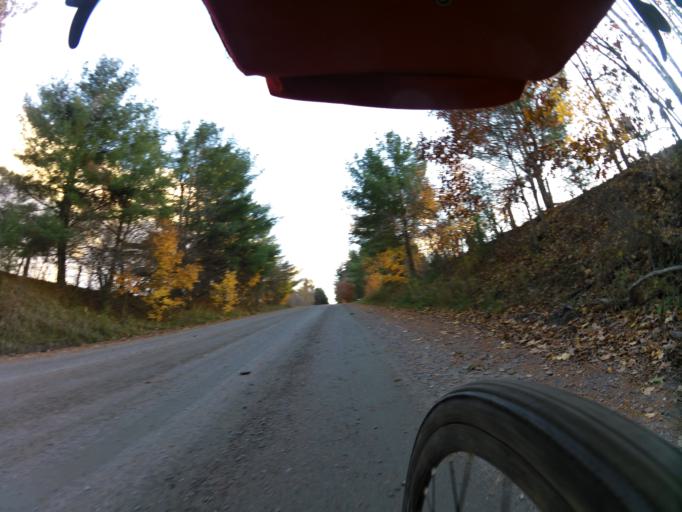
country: CA
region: Quebec
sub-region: Outaouais
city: Shawville
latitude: 45.6387
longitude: -76.3173
